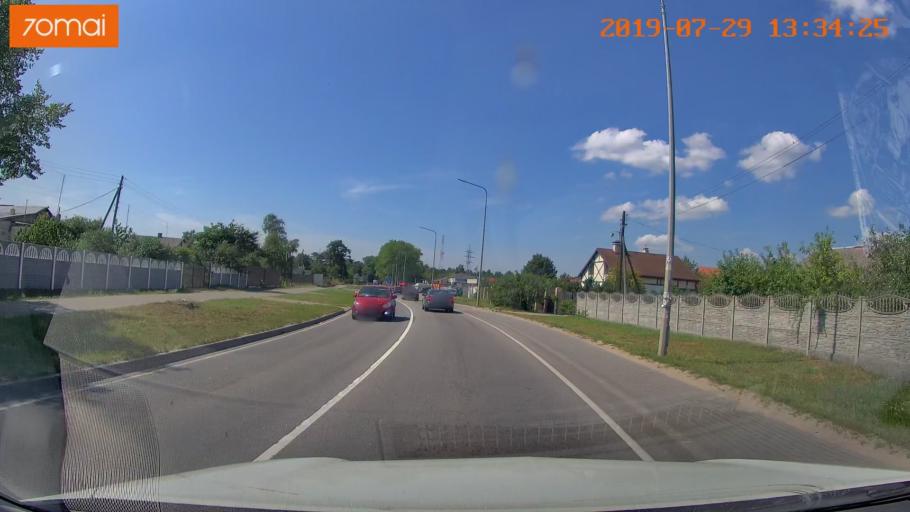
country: RU
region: Kaliningrad
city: Volochayevskoye
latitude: 54.7001
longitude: 20.2167
